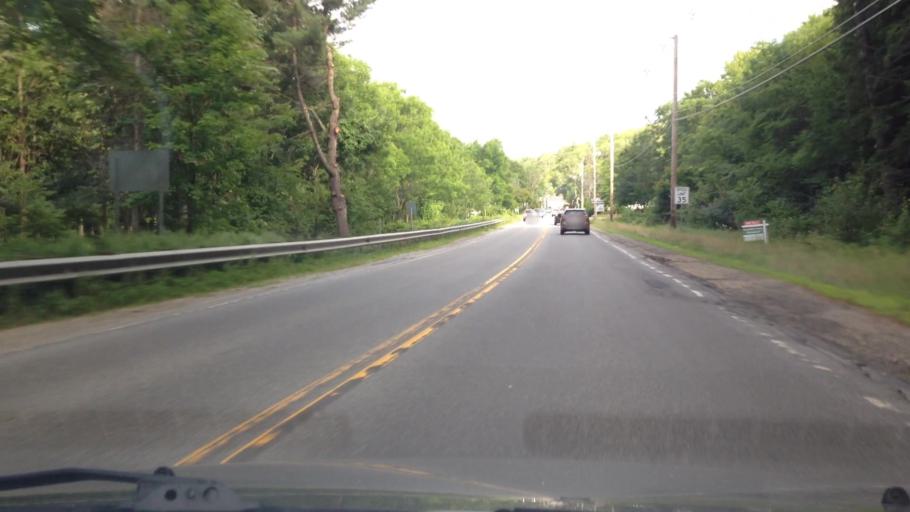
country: US
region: New Hampshire
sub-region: Cheshire County
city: Marlborough
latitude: 42.9128
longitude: -72.2244
